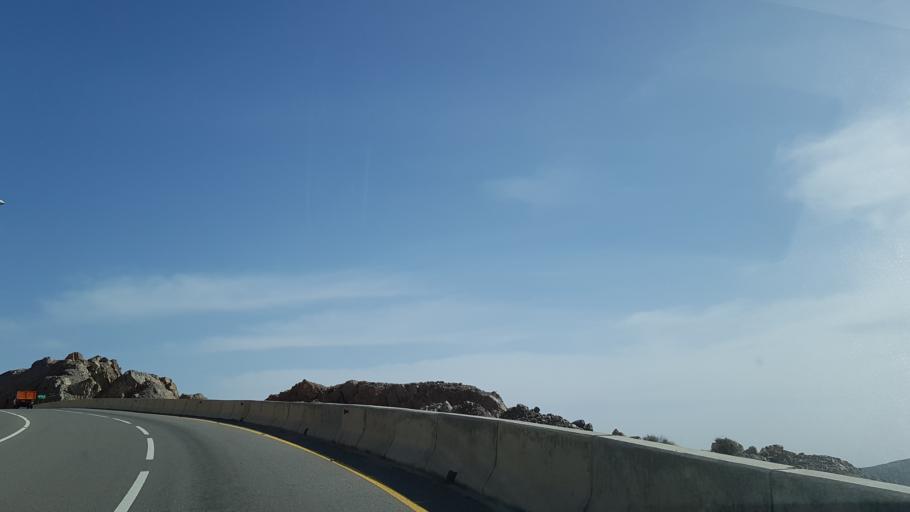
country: OM
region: Muhafazat ad Dakhiliyah
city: Izki
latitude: 23.0603
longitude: 57.7267
